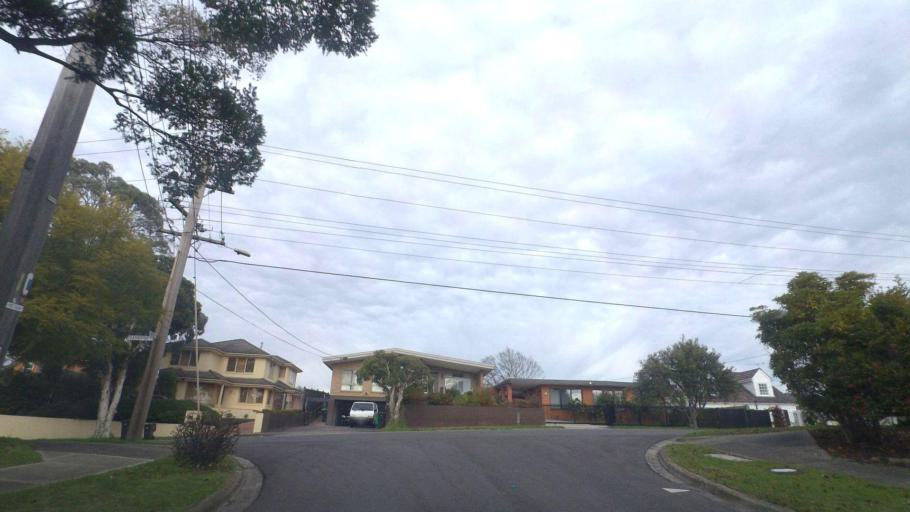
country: AU
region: Victoria
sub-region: Manningham
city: Templestowe Lower
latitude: -37.7679
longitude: 145.1104
